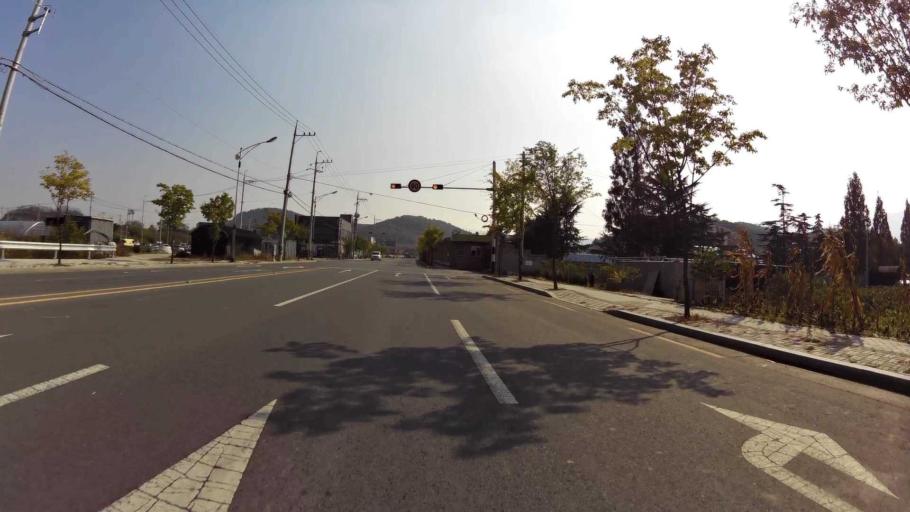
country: KR
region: Gyeongsangbuk-do
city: Gyeongsan-si
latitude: 35.8540
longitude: 128.6815
